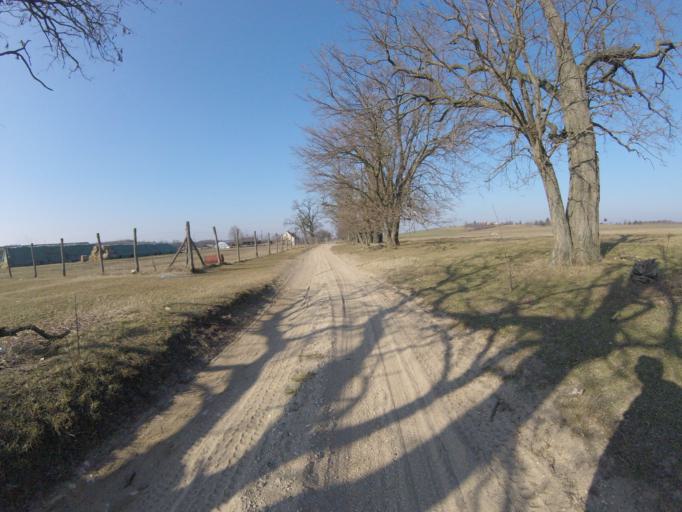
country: HU
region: Komarom-Esztergom
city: Oroszlany
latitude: 47.4698
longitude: 18.3375
